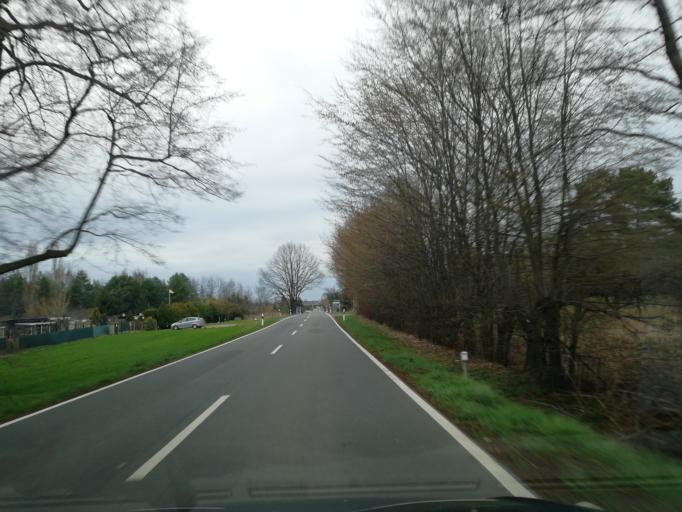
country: DE
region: Brandenburg
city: Vetschau
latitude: 51.7734
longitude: 14.0687
